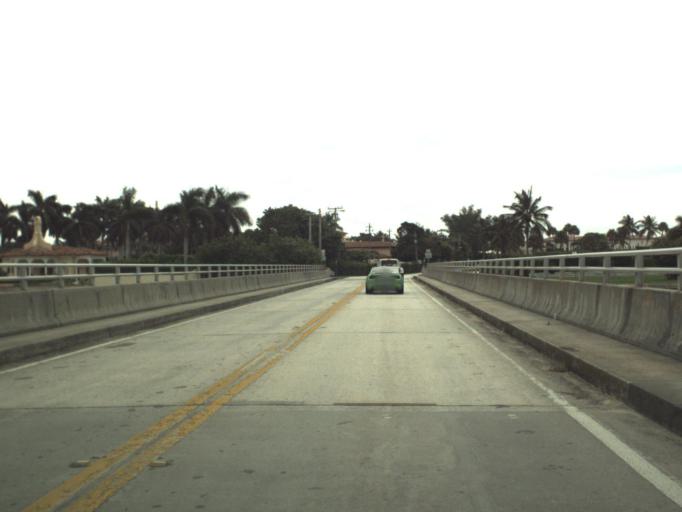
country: US
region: Florida
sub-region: Palm Beach County
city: Palm Beach
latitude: 26.6757
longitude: -80.0409
